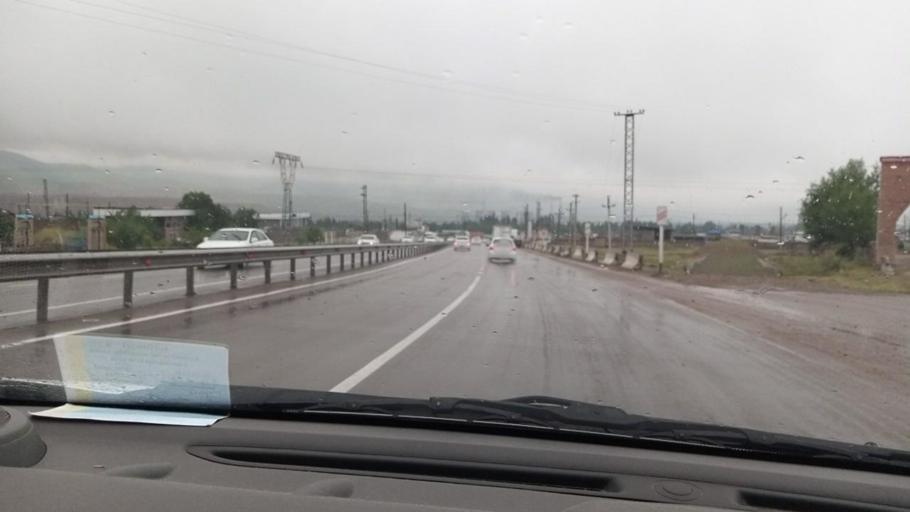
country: UZ
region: Toshkent
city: Angren
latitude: 41.0309
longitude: 70.1379
